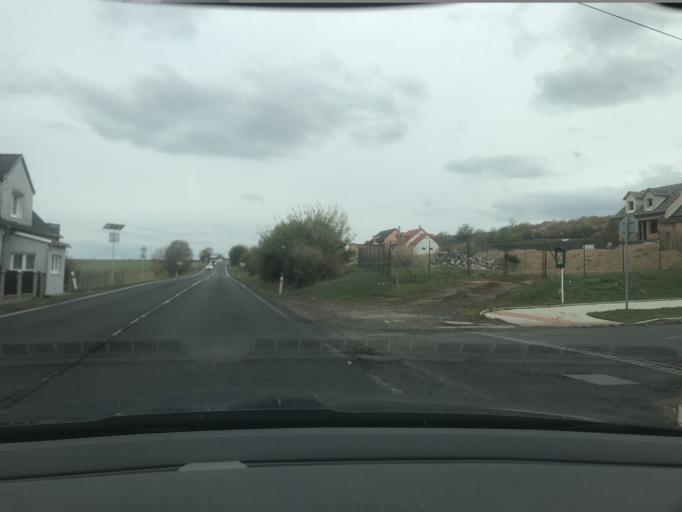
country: CZ
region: Ustecky
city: Cizkovice
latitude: 50.4891
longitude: 14.0209
